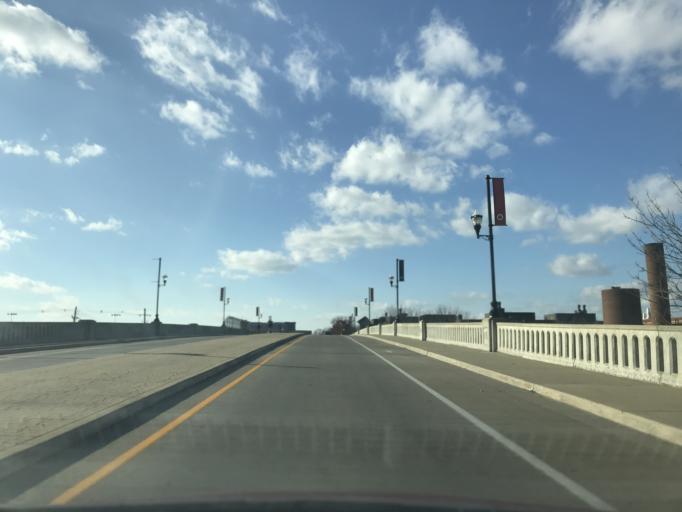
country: US
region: Kentucky
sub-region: Jefferson County
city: Audubon Park
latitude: 38.2132
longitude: -85.7554
